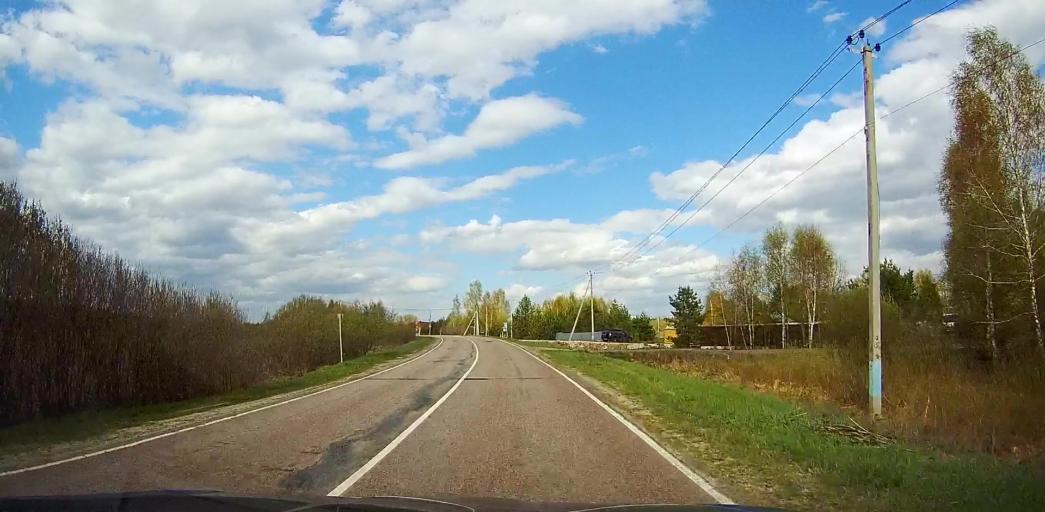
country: RU
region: Moskovskaya
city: Rakhmanovo
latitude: 55.6692
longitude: 38.6454
